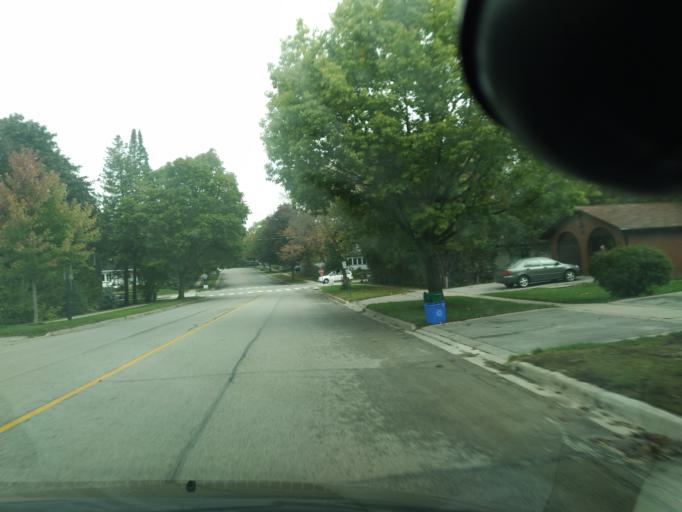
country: CA
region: Ontario
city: Newmarket
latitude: 44.0568
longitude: -79.4425
